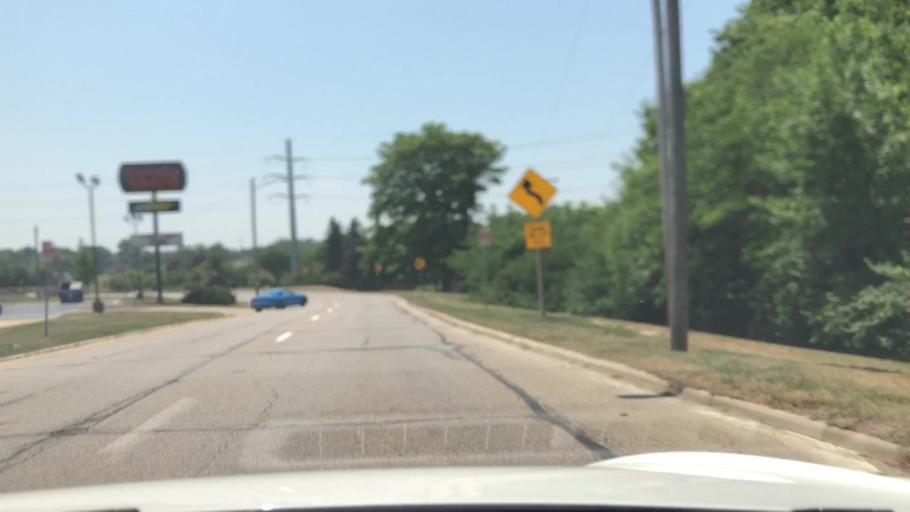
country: US
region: Illinois
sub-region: McLean County
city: Bloomington
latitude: 40.4630
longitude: -88.9939
